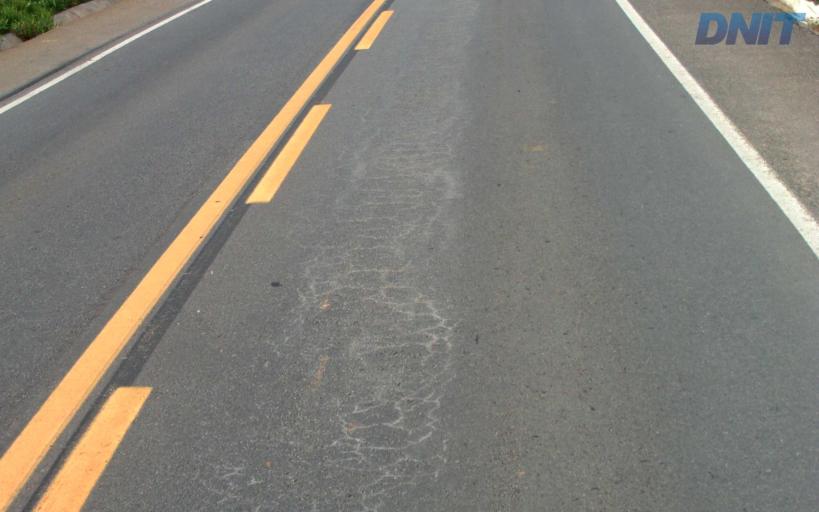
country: BR
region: Minas Gerais
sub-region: Belo Oriente
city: Belo Oriente
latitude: -19.1824
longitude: -42.2622
